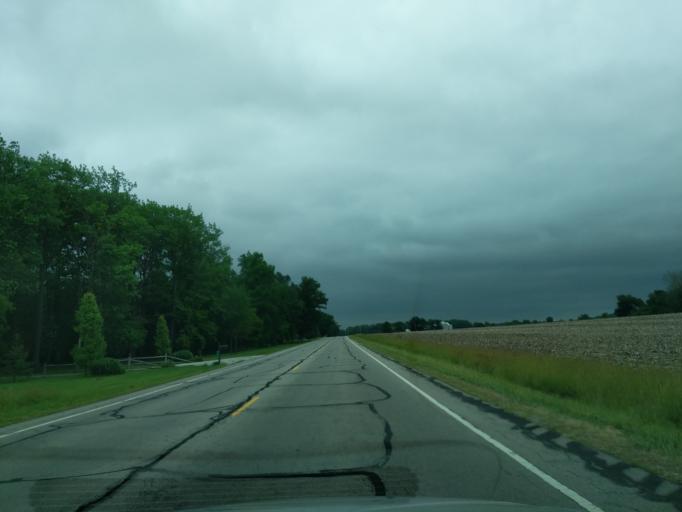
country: US
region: Indiana
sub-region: Madison County
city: Alexandria
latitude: 40.2774
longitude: -85.6210
